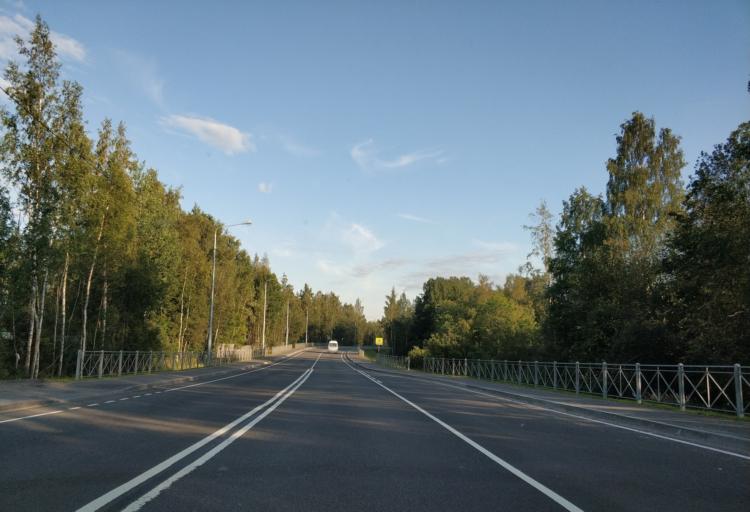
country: RU
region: Leningrad
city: Sapernoye
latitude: 60.7032
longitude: 29.9702
